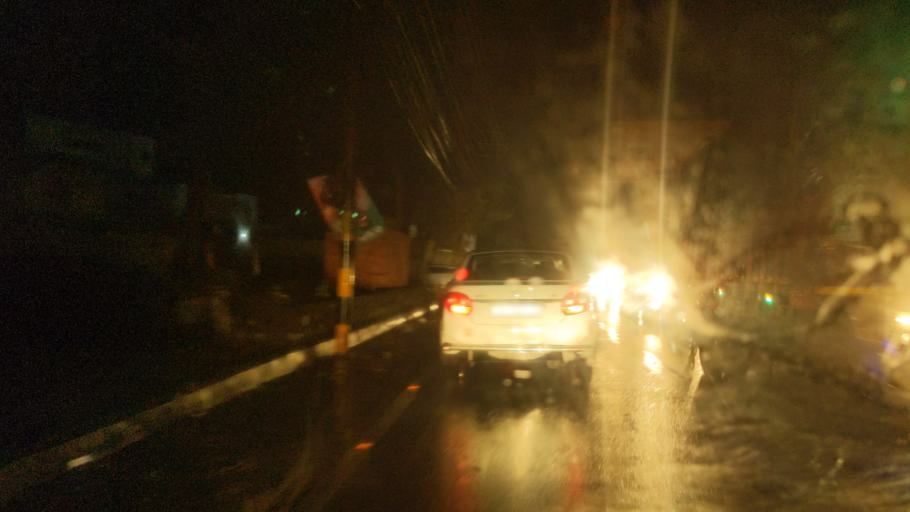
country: IN
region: Uttarakhand
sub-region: Naini Tal
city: Haldwani
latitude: 29.2732
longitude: 79.5449
